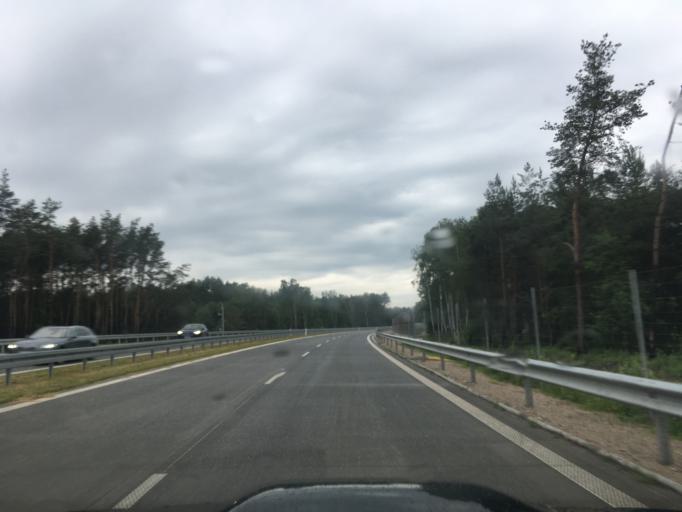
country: PL
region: Masovian Voivodeship
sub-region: Powiat piaseczynski
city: Gora Kalwaria
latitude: 51.9808
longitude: 21.1786
